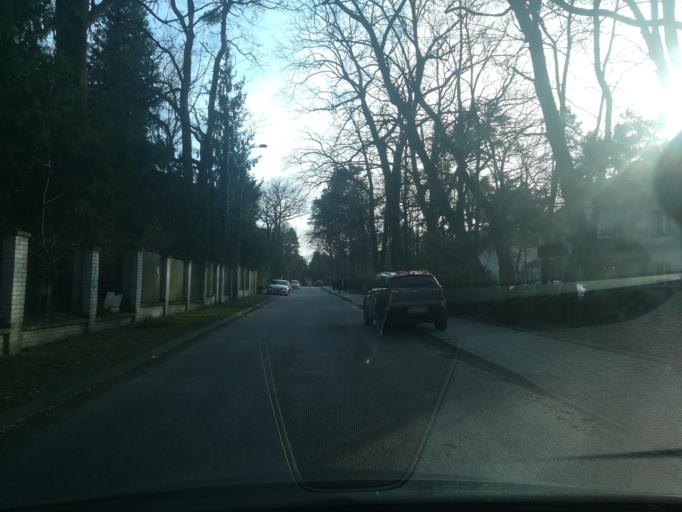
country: PL
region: Masovian Voivodeship
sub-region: Powiat piaseczynski
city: Konstancin-Jeziorna
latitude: 52.0836
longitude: 21.1257
